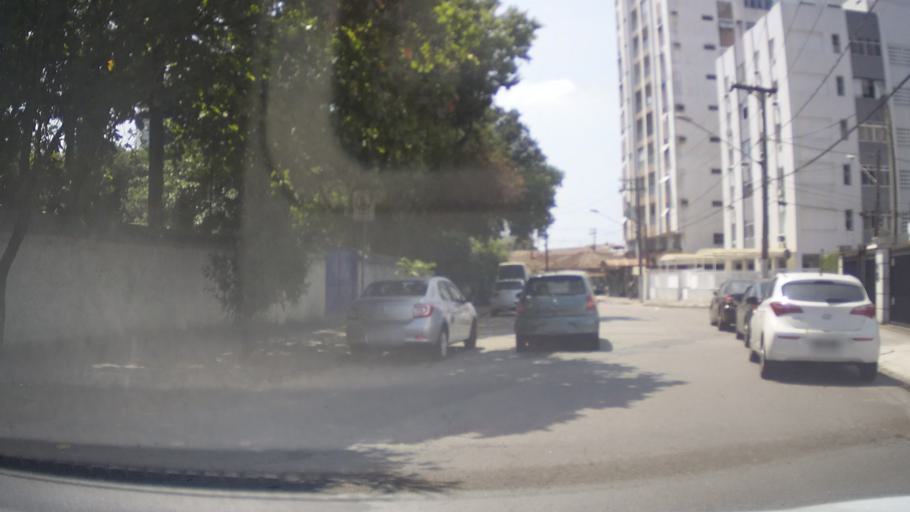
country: BR
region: Sao Paulo
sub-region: Santos
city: Santos
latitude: -23.9786
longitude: -46.2999
